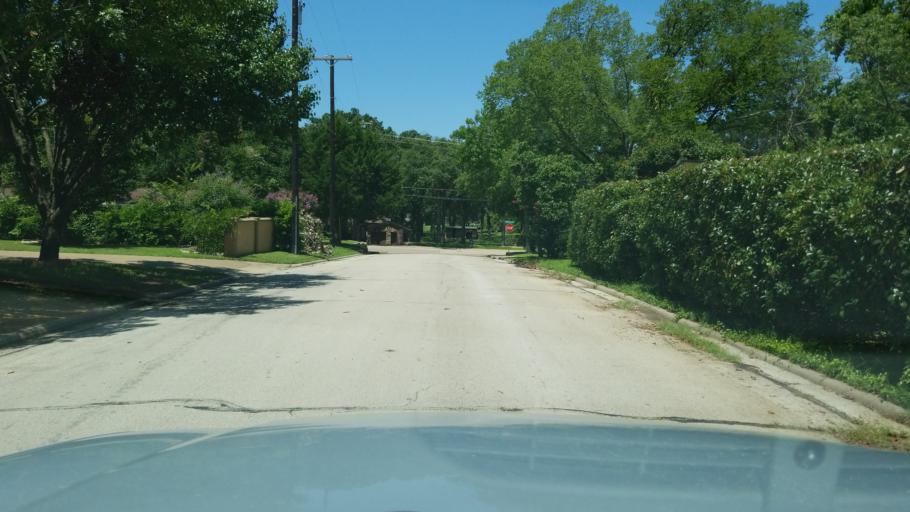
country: US
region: Texas
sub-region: Dallas County
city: Irving
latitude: 32.8065
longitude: -96.9161
